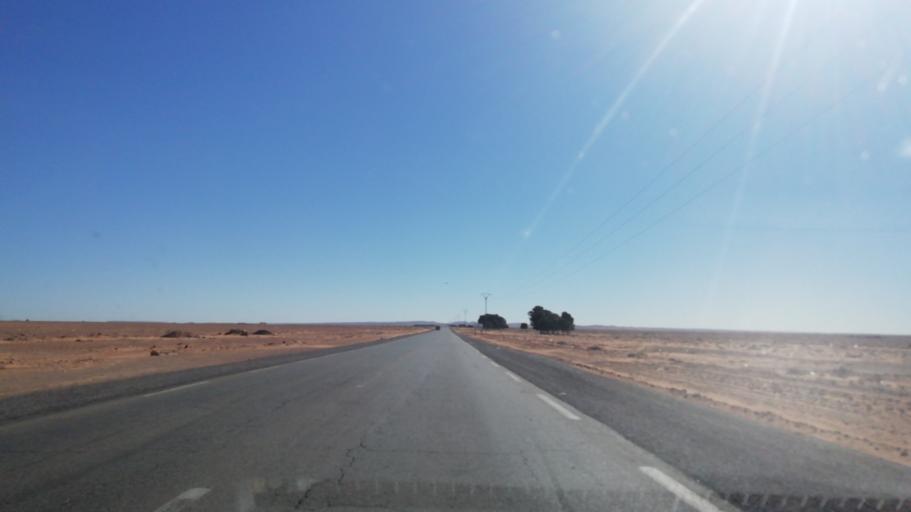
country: DZ
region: Saida
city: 'Ain el Hadjar
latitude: 34.0099
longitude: 0.1187
